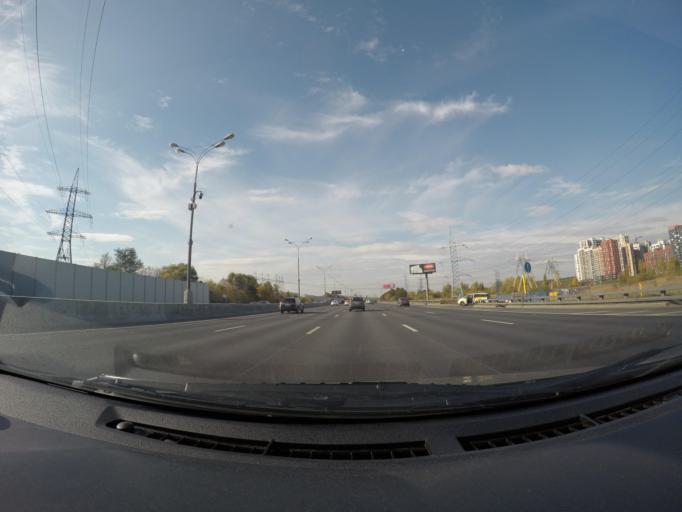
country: RU
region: Moscow
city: Kozeyevo
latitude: 55.8972
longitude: 37.6450
